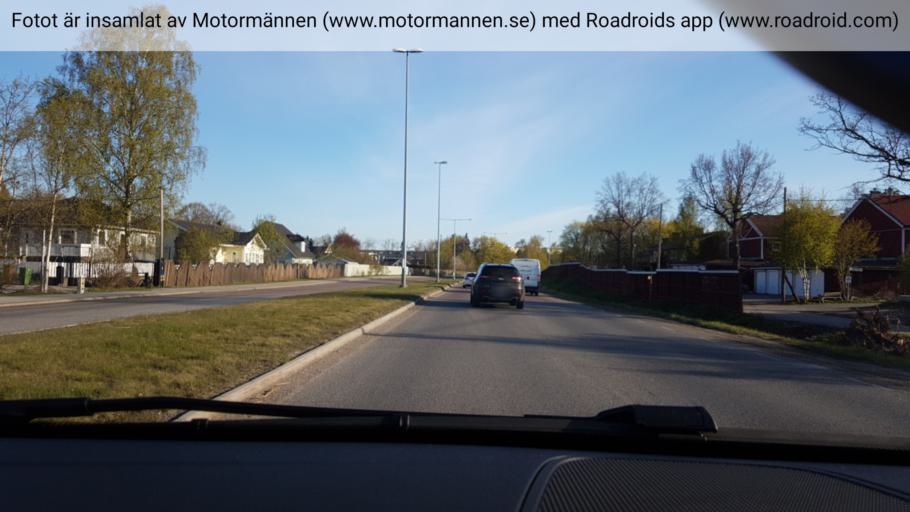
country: SE
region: Stockholm
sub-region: Huddinge Kommun
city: Segeltorp
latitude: 59.2804
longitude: 17.9423
